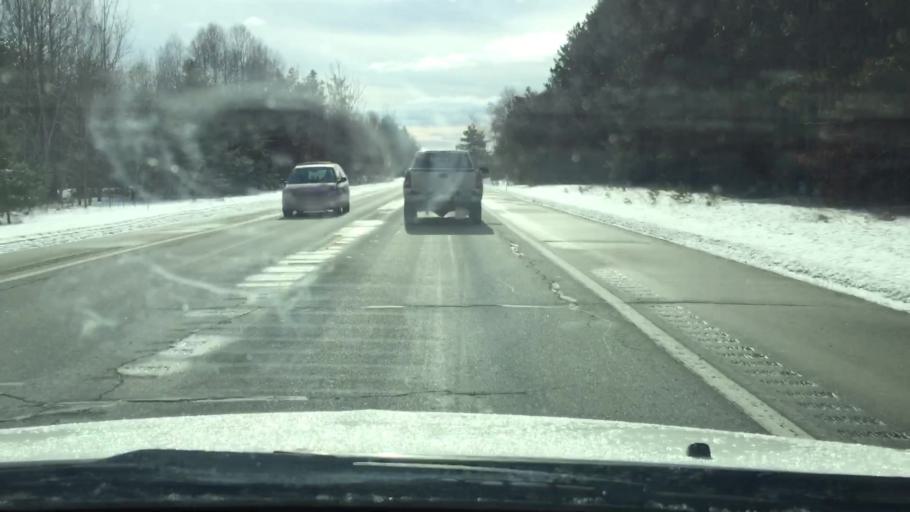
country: US
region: Michigan
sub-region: Kalkaska County
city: Kalkaska
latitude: 44.6041
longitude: -85.3247
